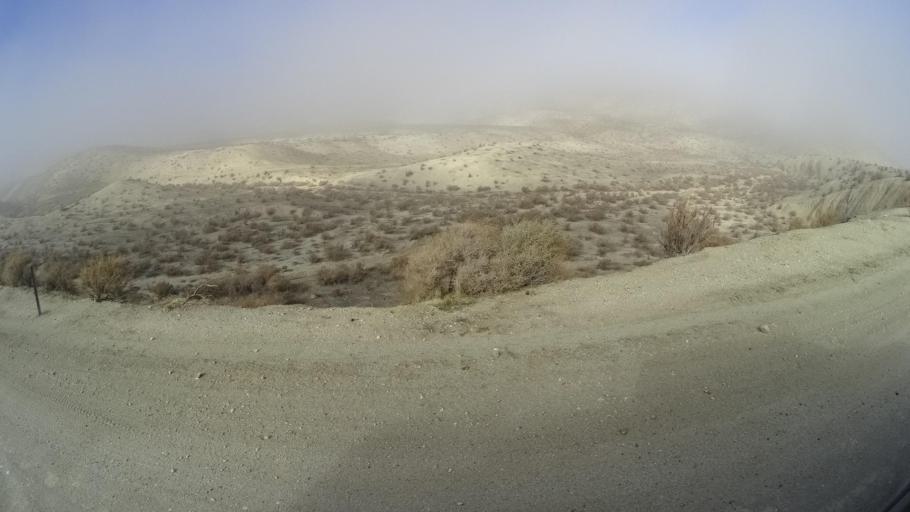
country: US
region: California
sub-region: Kern County
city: Maricopa
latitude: 35.0222
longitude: -119.4462
